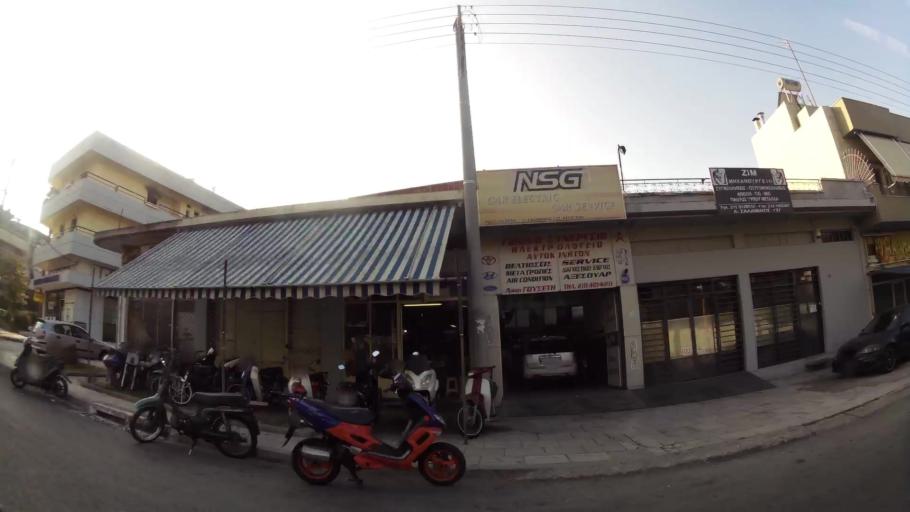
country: GR
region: Attica
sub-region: Nomos Piraios
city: Keratsini
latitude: 37.9643
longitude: 23.6212
